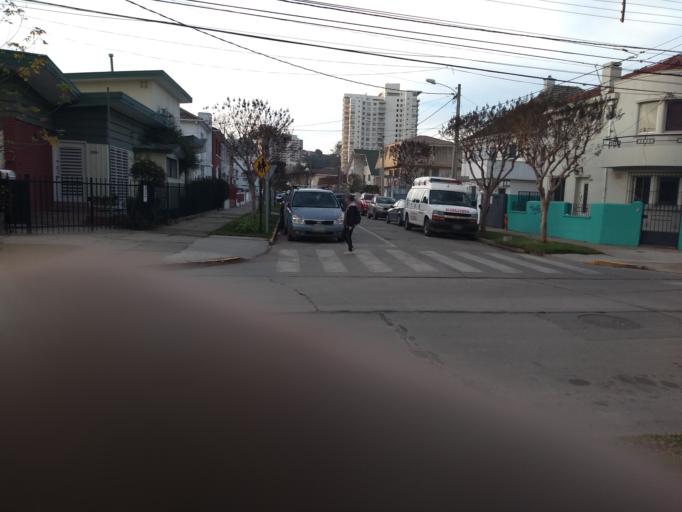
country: CL
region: Valparaiso
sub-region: Provincia de Valparaiso
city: Vina del Mar
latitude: -33.0218
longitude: -71.5426
